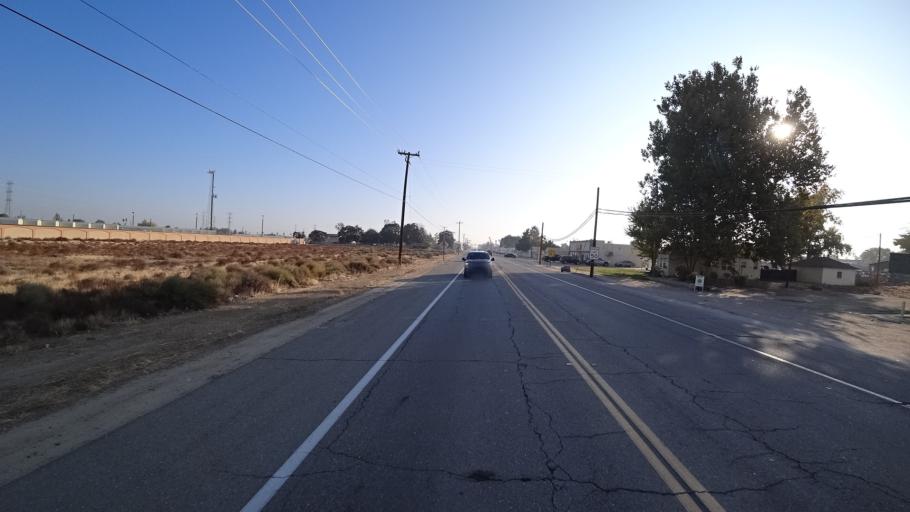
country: US
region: California
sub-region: Kern County
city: Rosedale
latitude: 35.3836
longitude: -119.1595
